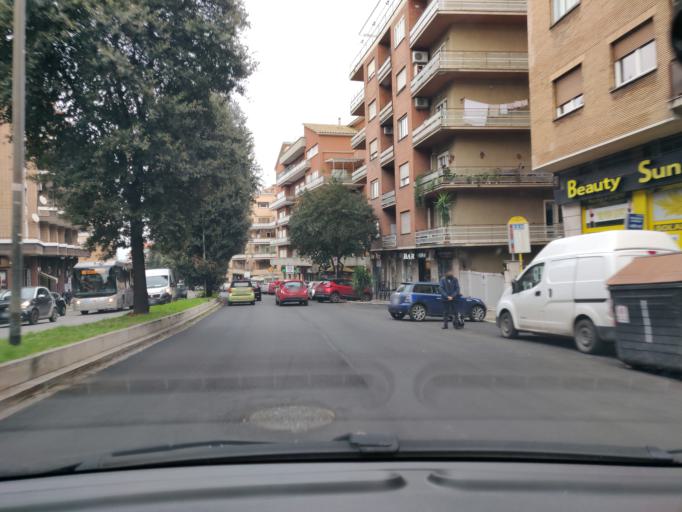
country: VA
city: Vatican City
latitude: 41.8994
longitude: 12.4355
